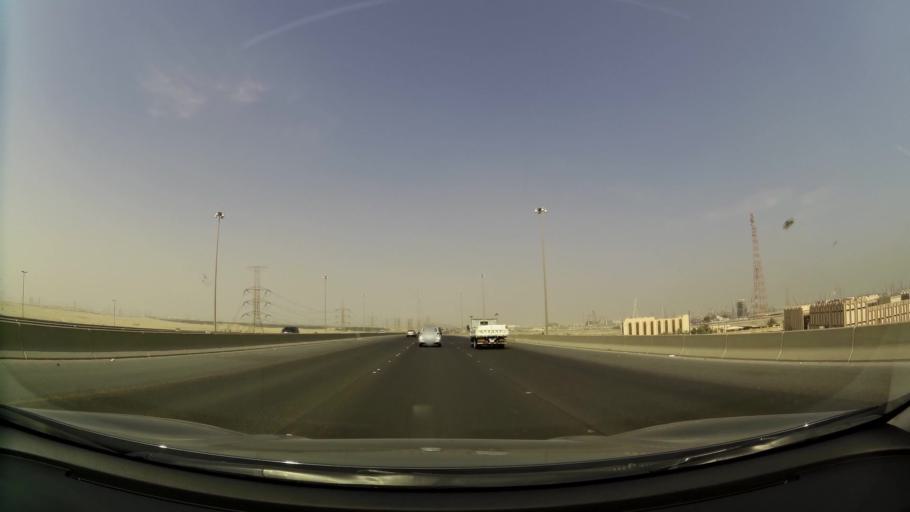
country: KW
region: Al Ahmadi
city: Al Fahahil
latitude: 29.0371
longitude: 48.1184
